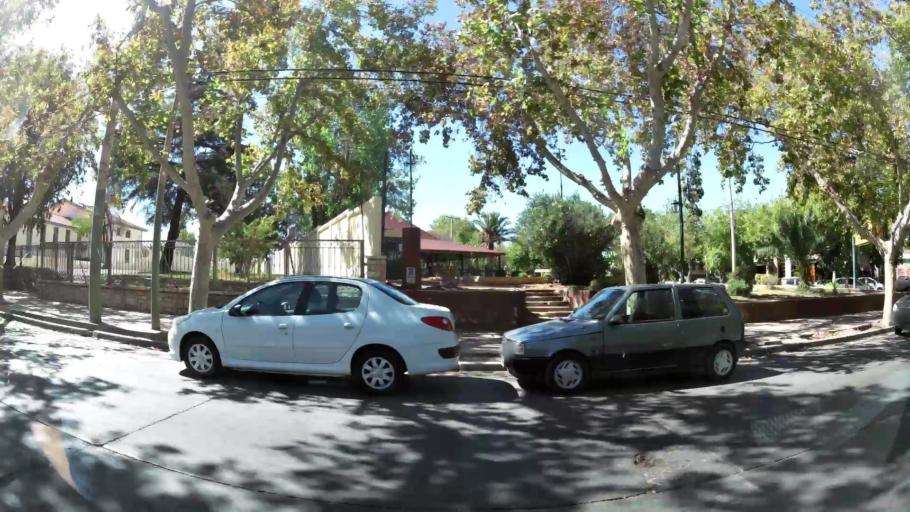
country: AR
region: San Juan
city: San Juan
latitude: -31.5312
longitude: -68.5529
